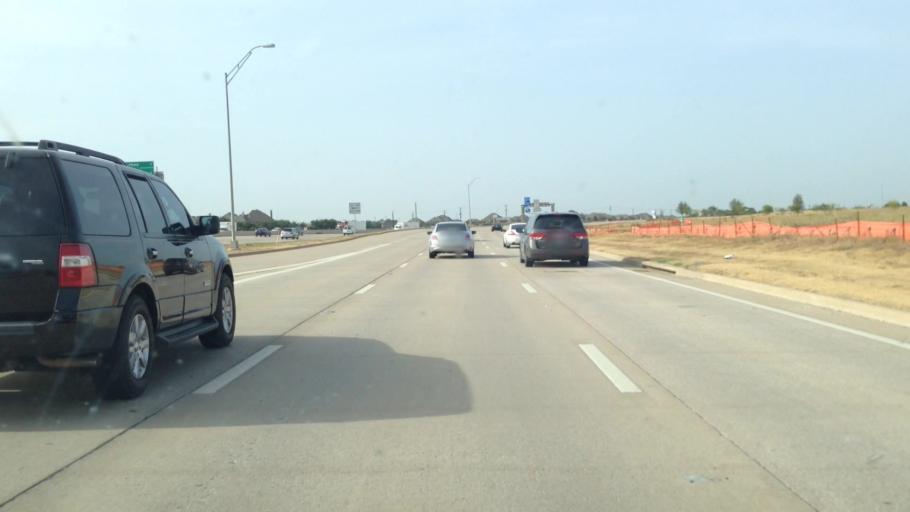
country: US
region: Texas
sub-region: Denton County
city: The Colony
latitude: 33.0416
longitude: -96.9235
